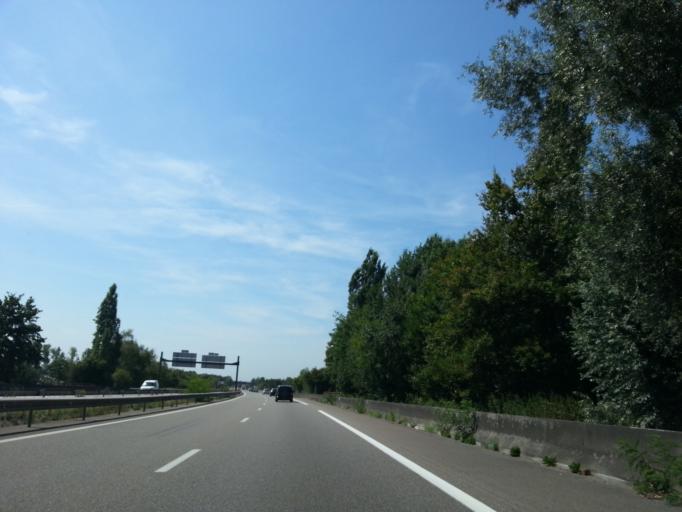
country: FR
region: Alsace
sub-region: Departement du Bas-Rhin
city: Niedernai
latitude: 48.4516
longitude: 7.5070
